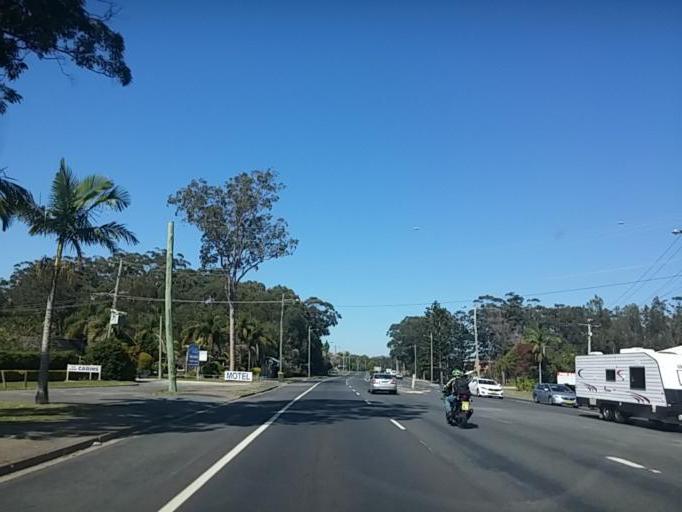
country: AU
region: New South Wales
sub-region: Coffs Harbour
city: Coffs Harbour
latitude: -30.2854
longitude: 153.1255
